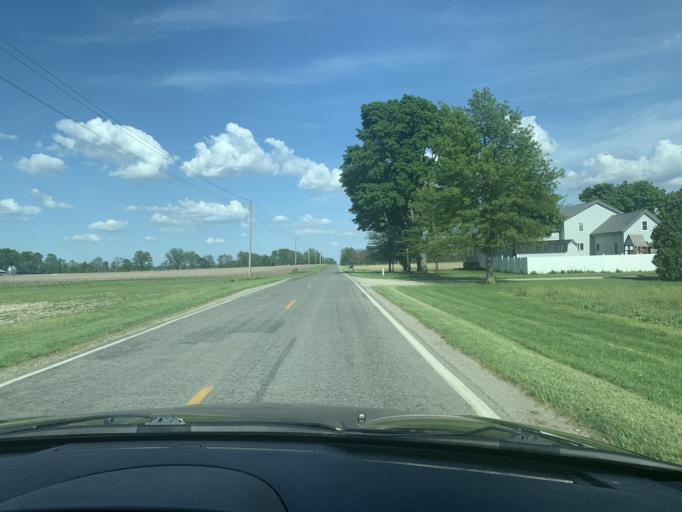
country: US
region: Ohio
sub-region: Logan County
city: De Graff
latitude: 40.2427
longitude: -83.9888
